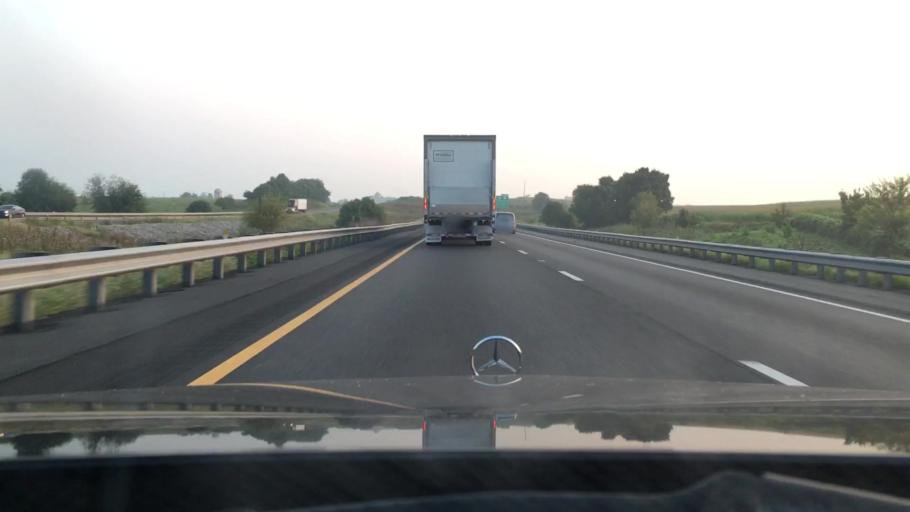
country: US
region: Virginia
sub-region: Shenandoah County
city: New Market
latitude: 38.6840
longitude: -78.6577
